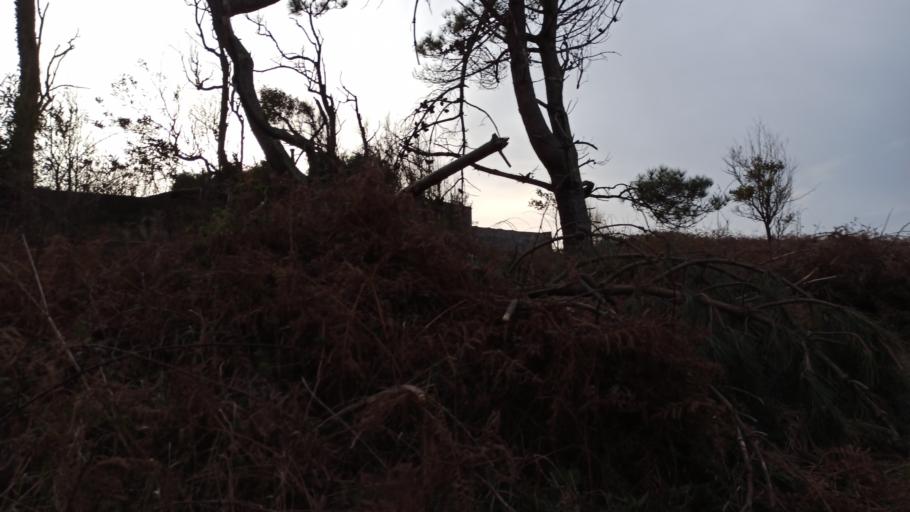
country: ES
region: Galicia
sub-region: Provincia da Coruna
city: Oleiros
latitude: 43.3996
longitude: -8.3327
